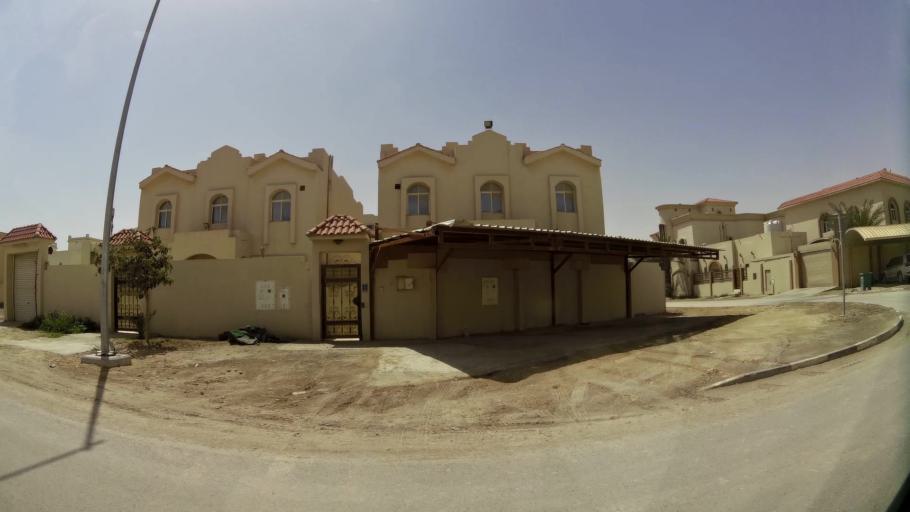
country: QA
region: Baladiyat Umm Salal
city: Umm Salal Muhammad
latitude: 25.3742
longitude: 51.4482
